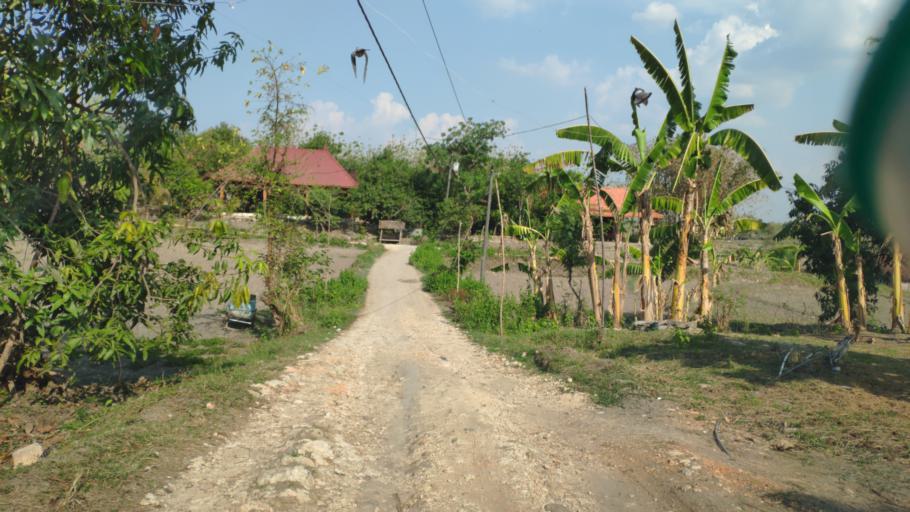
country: ID
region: Central Java
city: Randublatung
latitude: -7.2425
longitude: 111.3321
